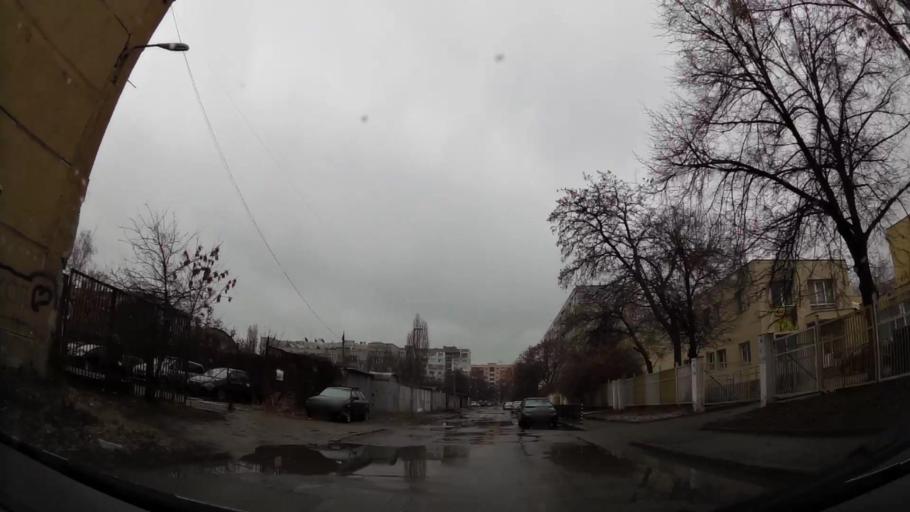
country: BG
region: Sofia-Capital
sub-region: Stolichna Obshtina
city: Sofia
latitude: 42.6708
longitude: 23.3894
